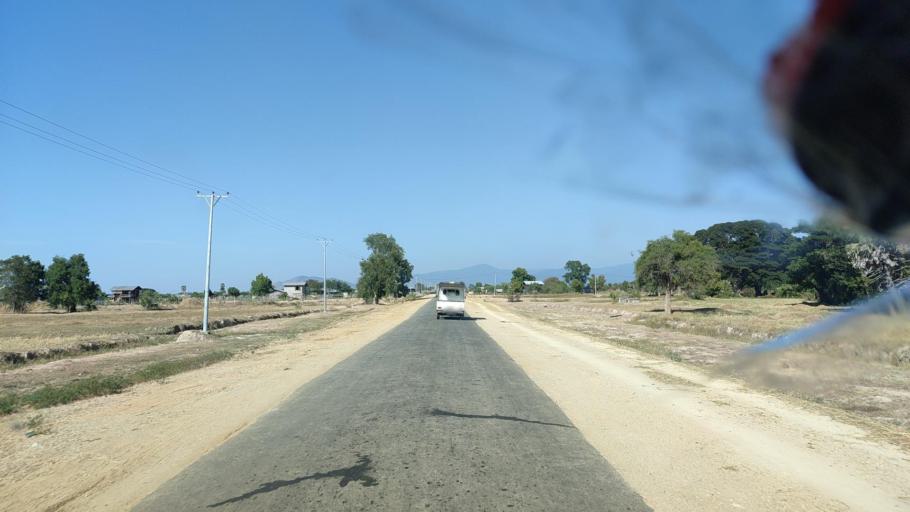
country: MM
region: Mandalay
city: Yamethin
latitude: 20.1651
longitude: 96.2593
